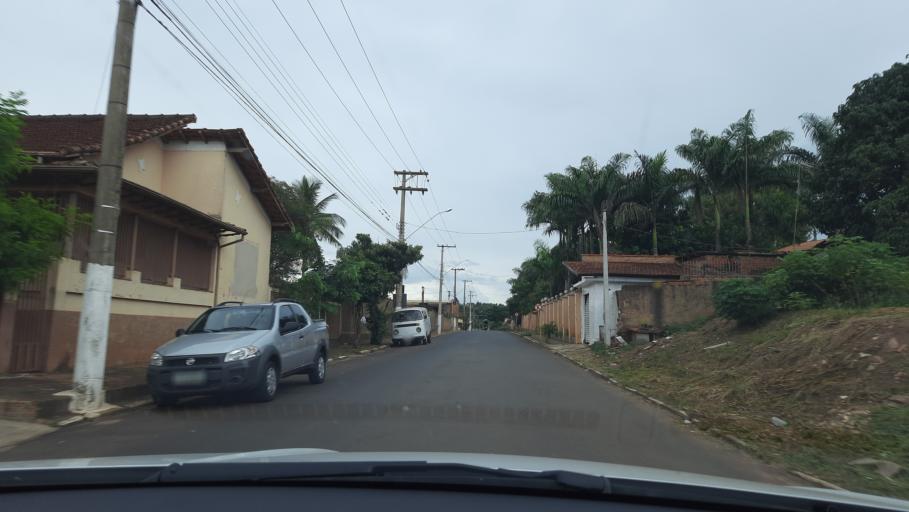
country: BR
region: Sao Paulo
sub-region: Casa Branca
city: Casa Branca
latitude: -21.7697
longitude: -47.0916
